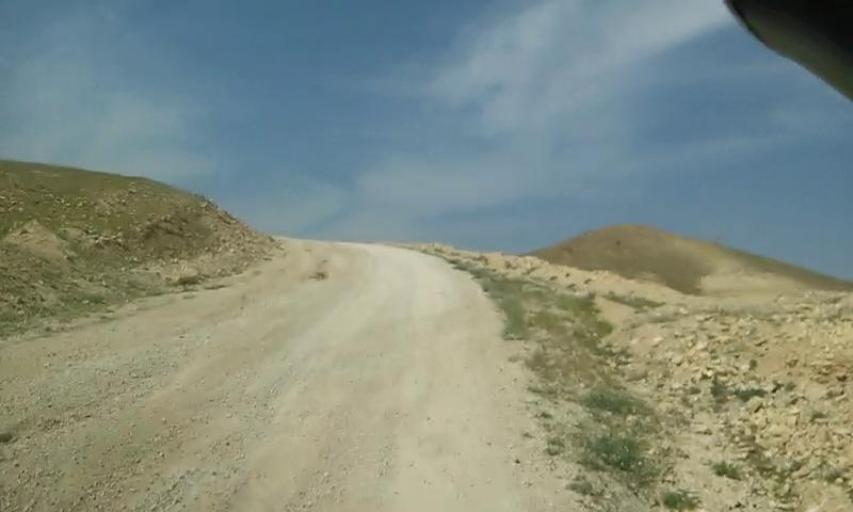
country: PS
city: `Arab ar Rashaydah
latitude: 31.4843
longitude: 35.2773
